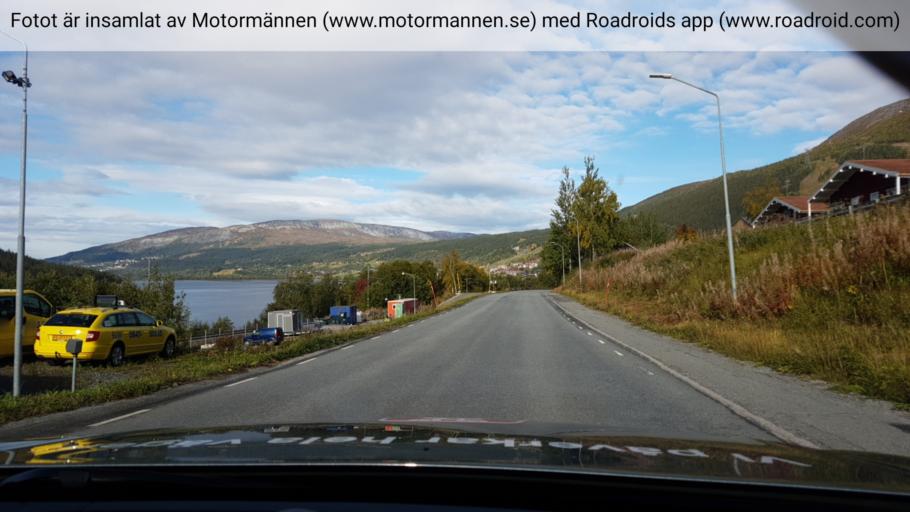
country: SE
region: Jaemtland
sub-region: Are Kommun
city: Are
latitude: 63.3904
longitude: 13.0961
